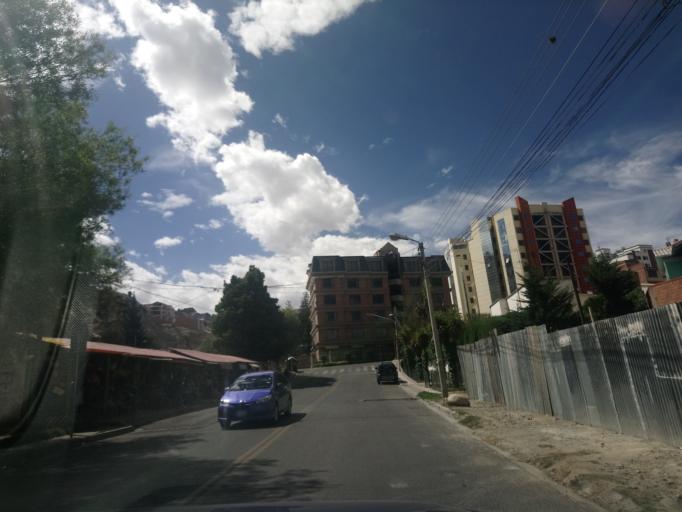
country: BO
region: La Paz
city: La Paz
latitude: -16.5263
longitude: -68.1121
